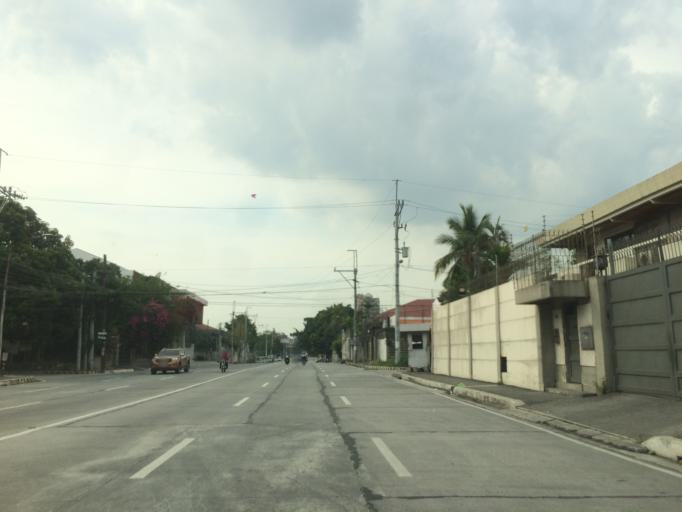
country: PH
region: Calabarzon
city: Del Monte
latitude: 14.6304
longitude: 121.0081
